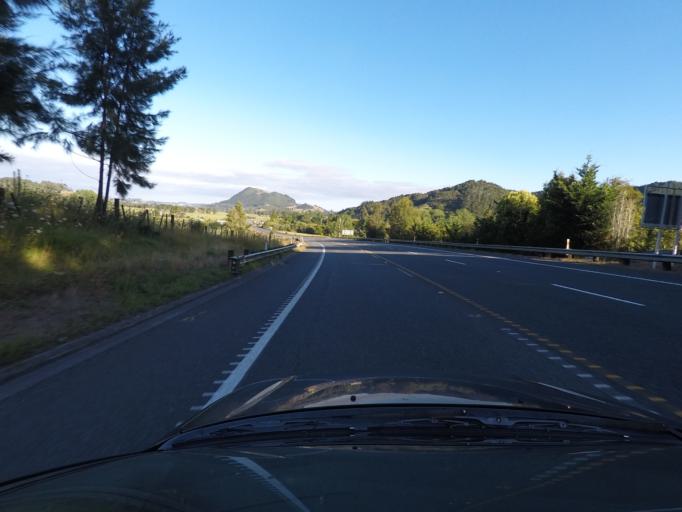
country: NZ
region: Northland
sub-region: Whangarei
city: Whangarei
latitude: -35.6277
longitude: 174.2956
